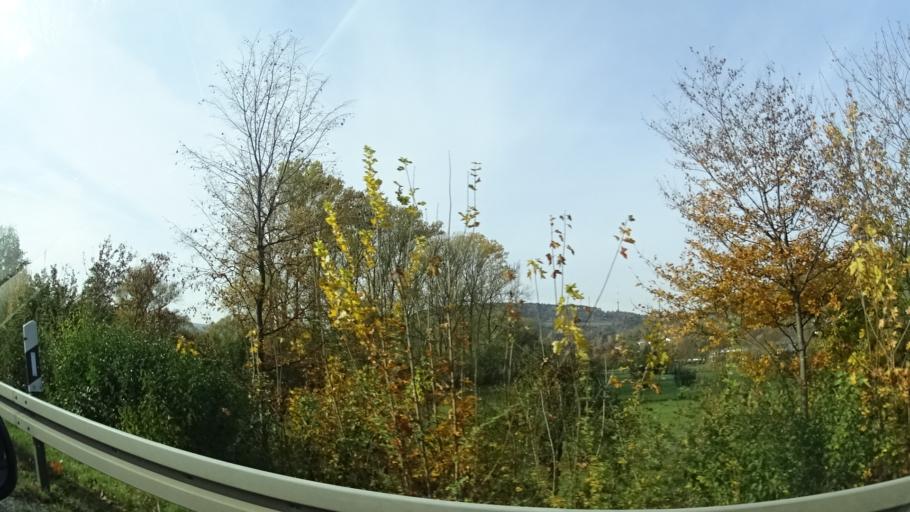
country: DE
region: Baden-Wuerttemberg
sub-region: Regierungsbezirk Stuttgart
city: Igersheim
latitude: 49.4935
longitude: 9.8096
